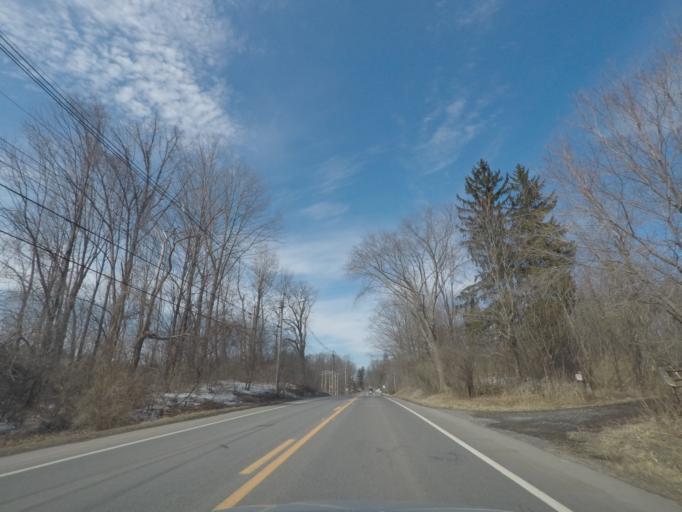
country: US
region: Massachusetts
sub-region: Berkshire County
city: West Stockbridge
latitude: 42.3265
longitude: -73.3619
